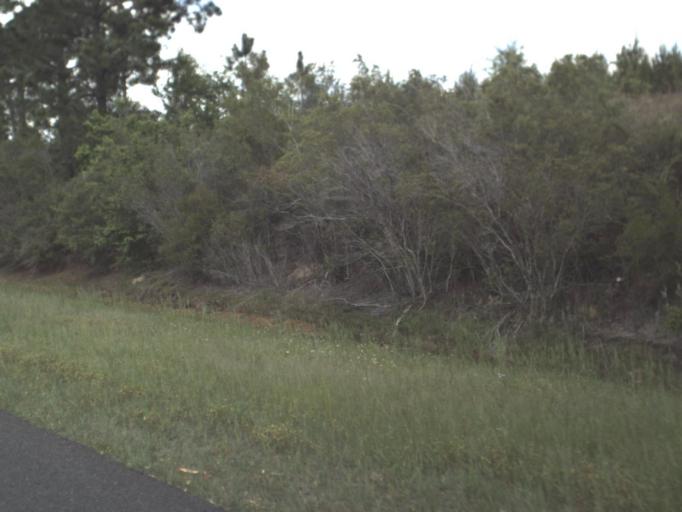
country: US
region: Florida
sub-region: Escambia County
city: Molino
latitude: 30.8027
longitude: -87.3360
